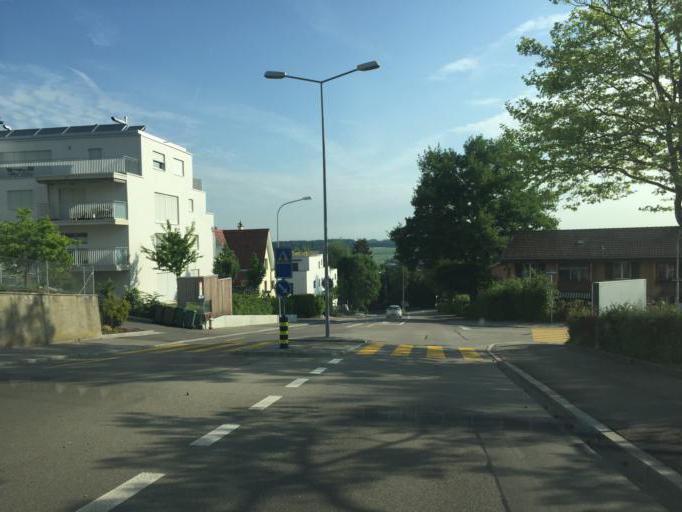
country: CH
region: Zurich
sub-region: Bezirk Zuerich
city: Zuerich (Kreis 11) / Affoltern
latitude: 47.4160
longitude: 8.5064
